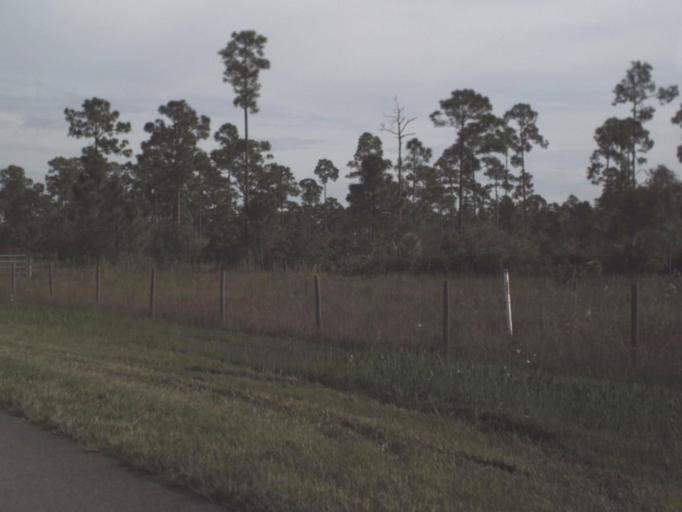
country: US
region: Florida
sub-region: Lee County
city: Olga
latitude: 26.9175
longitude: -81.7604
